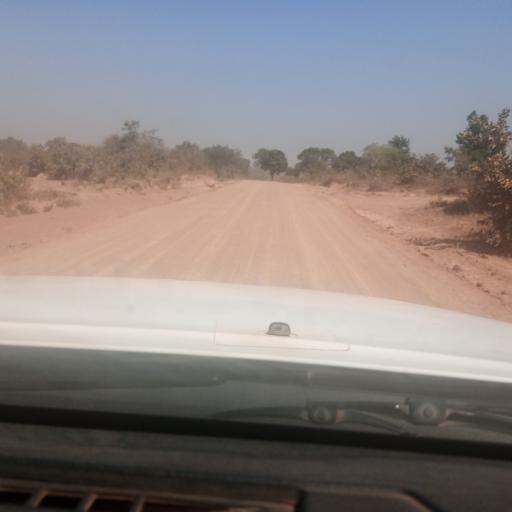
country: NG
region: Adamawa
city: Yola
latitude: 9.0964
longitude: 12.3899
